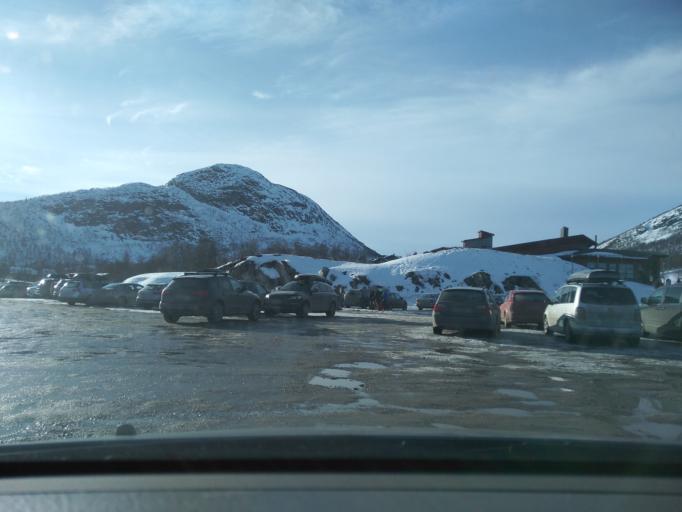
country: NO
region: Aust-Agder
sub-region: Bykle
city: Hovden
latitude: 59.5687
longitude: 7.3507
